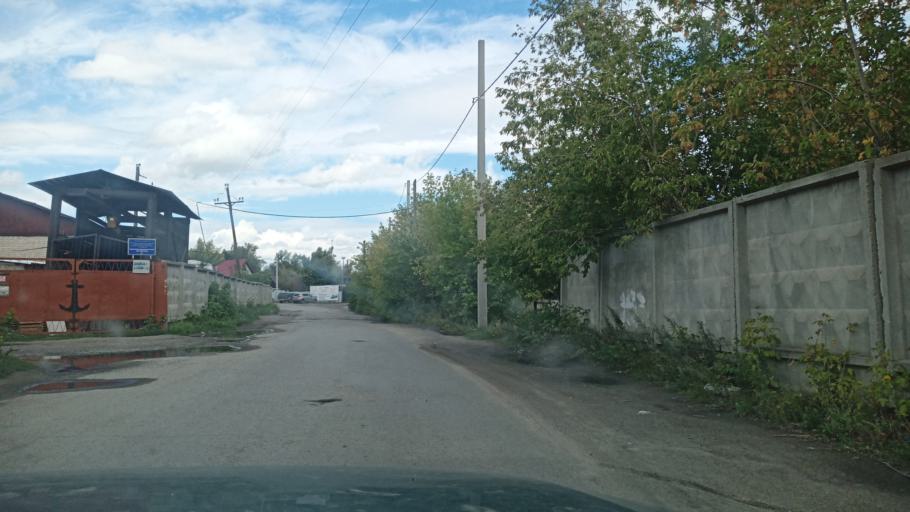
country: RU
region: Altai Krai
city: Zaton
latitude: 53.3334
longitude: 83.8069
